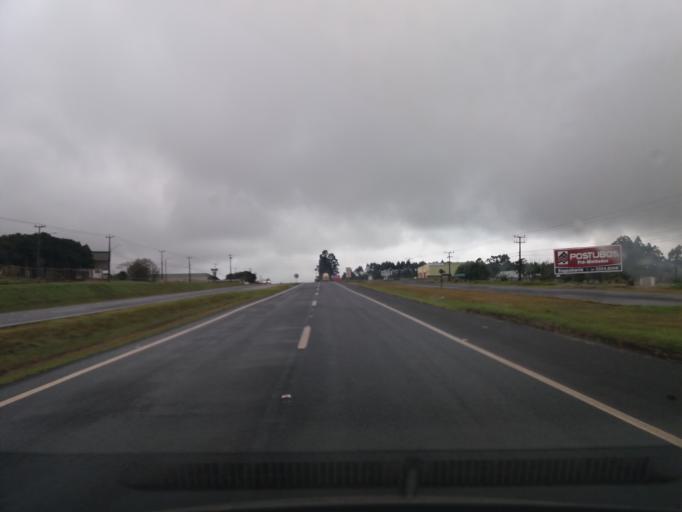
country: BR
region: Parana
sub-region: Cascavel
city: Cascavel
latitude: -24.9981
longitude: -53.5175
